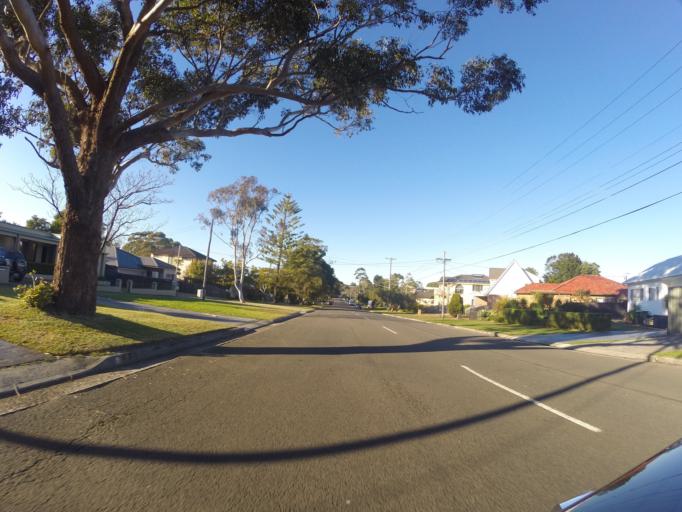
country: AU
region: New South Wales
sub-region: Sutherland Shire
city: Miranda
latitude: -34.0451
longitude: 151.1008
